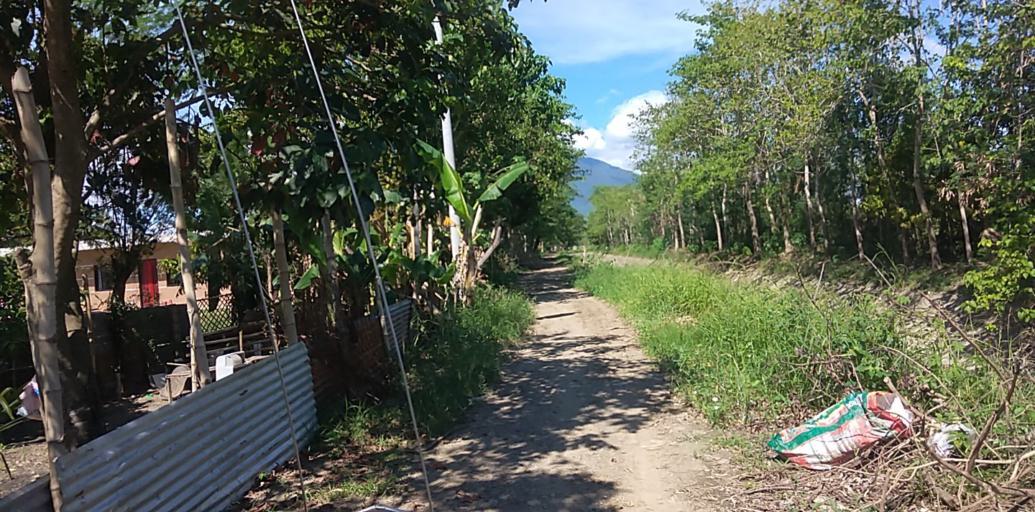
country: PH
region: Central Luzon
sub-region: Province of Pampanga
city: Arayat
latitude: 15.1284
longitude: 120.7811
